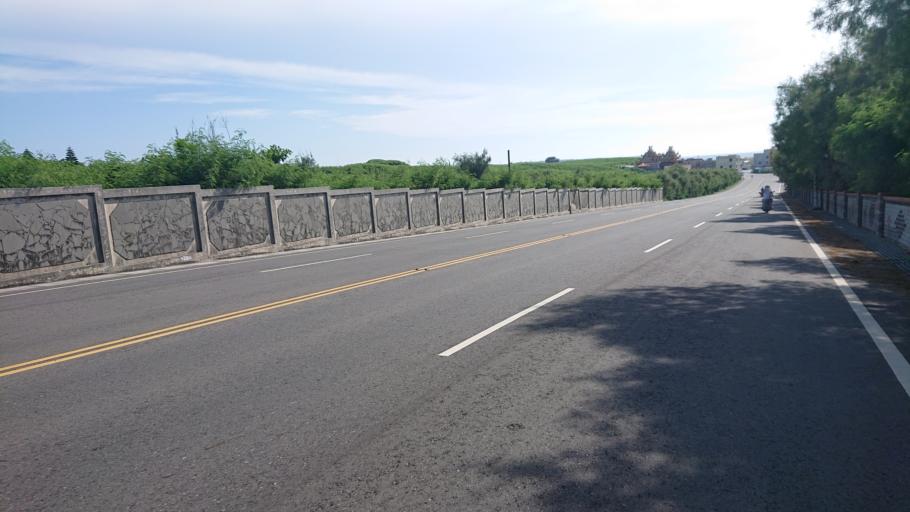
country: TW
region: Taiwan
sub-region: Penghu
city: Ma-kung
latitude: 23.5206
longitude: 119.5809
